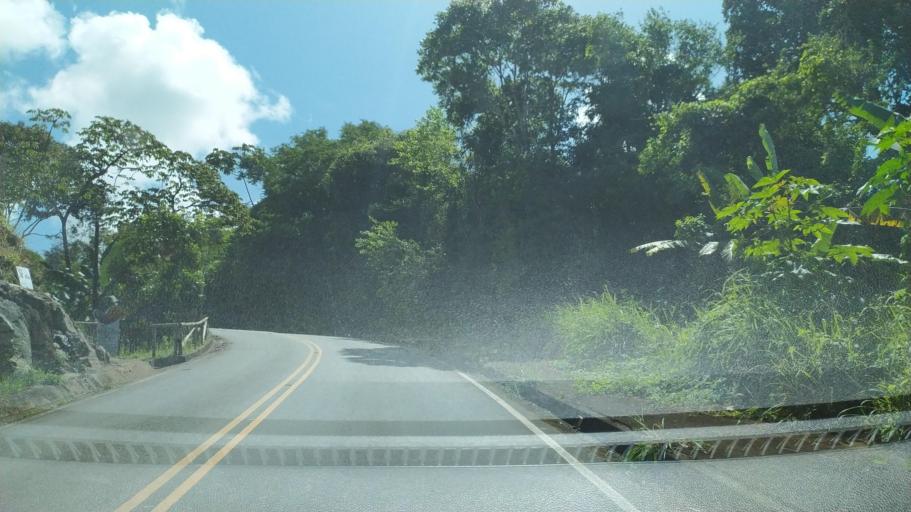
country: BR
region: Alagoas
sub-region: Uniao Dos Palmares
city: Uniao dos Palmares
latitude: -9.1659
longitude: -36.0661
